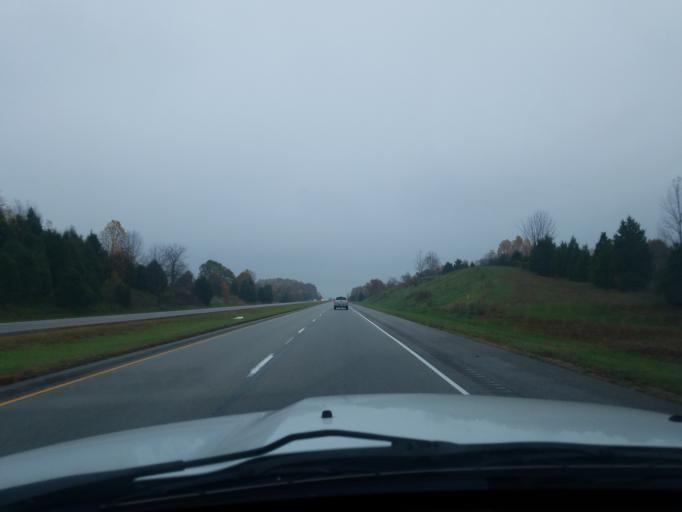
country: US
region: Kentucky
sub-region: Hardin County
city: Elizabethtown
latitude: 37.6357
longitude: -85.8306
